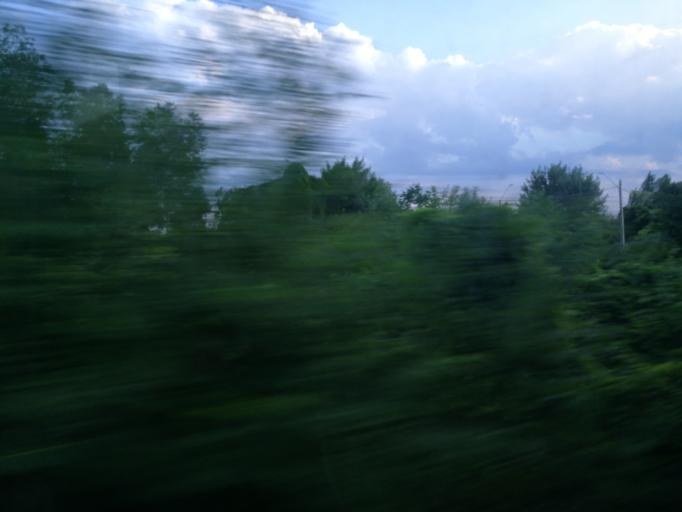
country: RO
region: Dambovita
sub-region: Comuna Branistea
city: Dambovicioara
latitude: 44.6622
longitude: 25.5626
